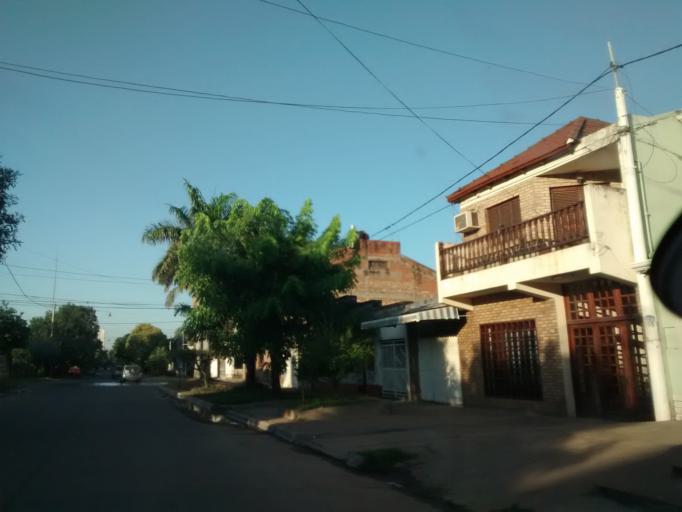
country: AR
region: Chaco
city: Resistencia
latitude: -27.4483
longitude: -58.9711
